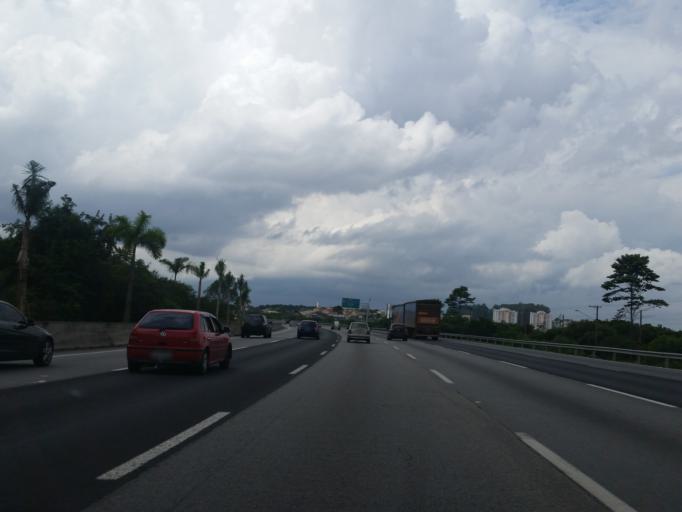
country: BR
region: Sao Paulo
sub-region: Guarulhos
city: Guarulhos
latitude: -23.4928
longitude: -46.5137
